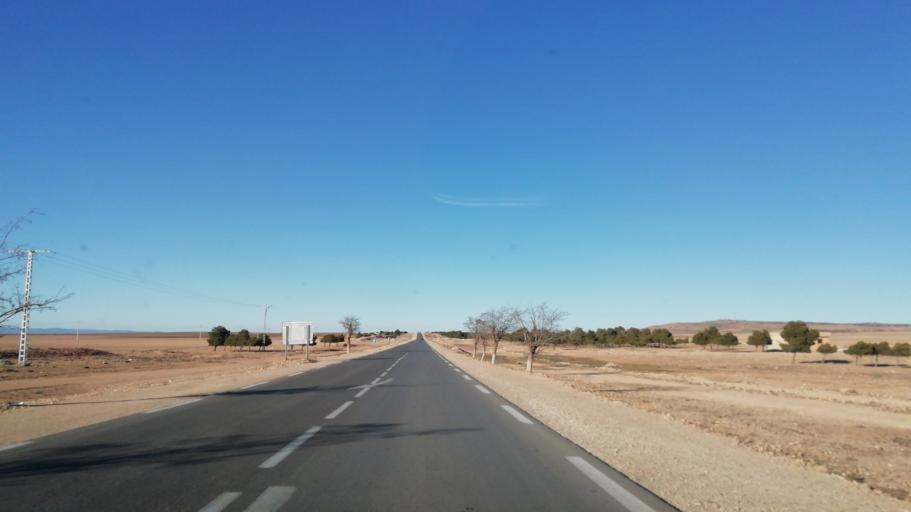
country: DZ
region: Tlemcen
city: Sebdou
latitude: 34.2346
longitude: -1.2565
